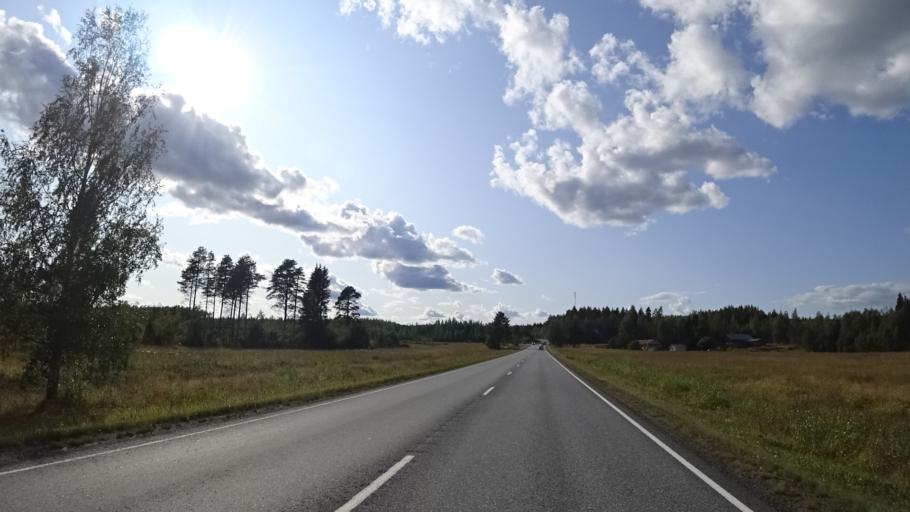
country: FI
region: North Karelia
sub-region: Keski-Karjala
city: Kitee
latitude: 62.0909
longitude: 29.9655
